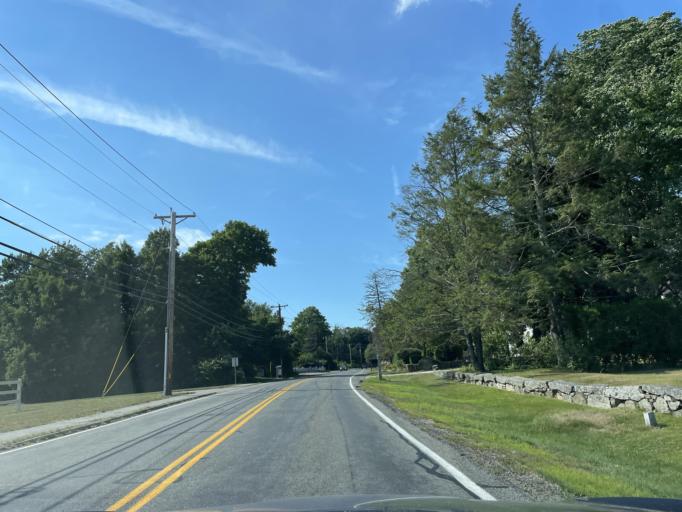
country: US
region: Massachusetts
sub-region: Worcester County
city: Mendon
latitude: 42.1154
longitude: -71.5623
